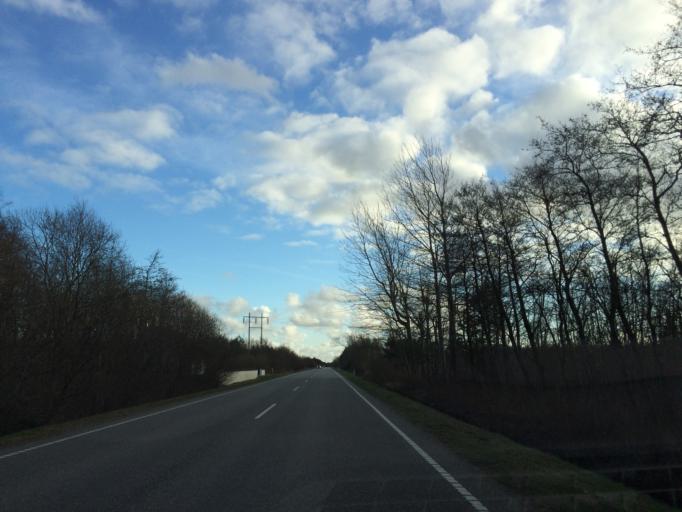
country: DK
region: Central Jutland
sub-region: Holstebro Kommune
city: Ulfborg
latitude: 56.3776
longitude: 8.3290
